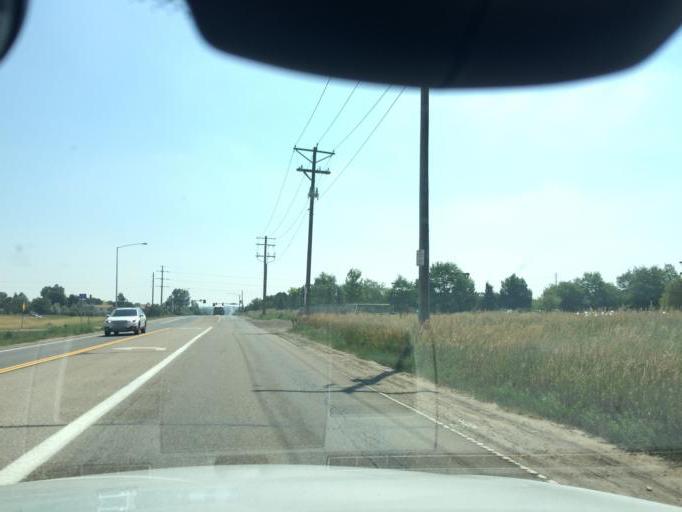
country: US
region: Colorado
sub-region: Broomfield County
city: Broomfield
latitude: 39.8998
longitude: -105.0754
